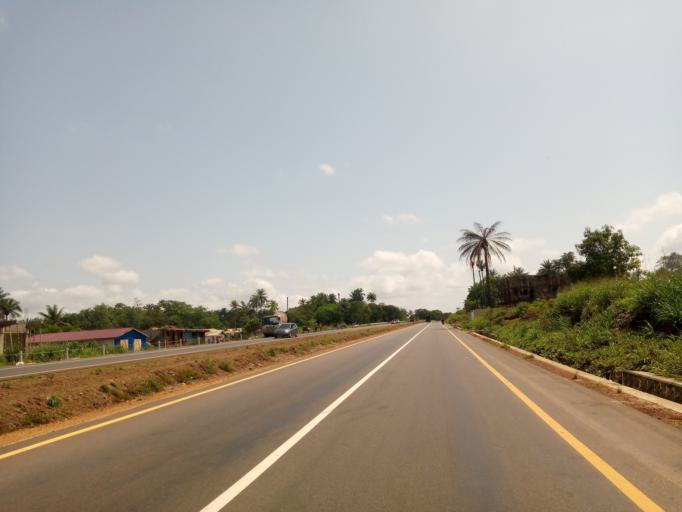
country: SL
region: Western Area
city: Waterloo
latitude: 8.3745
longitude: -12.9588
